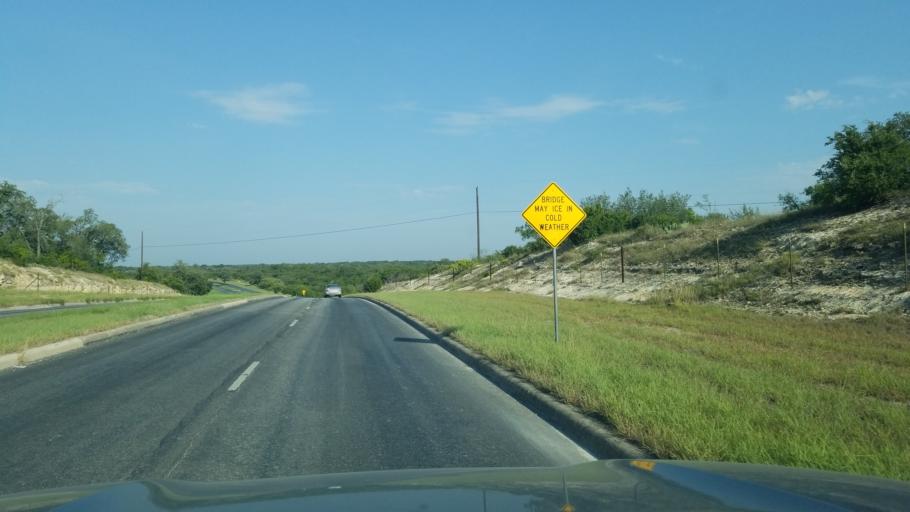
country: US
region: Texas
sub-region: Bexar County
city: Helotes
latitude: 29.4620
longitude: -98.7497
